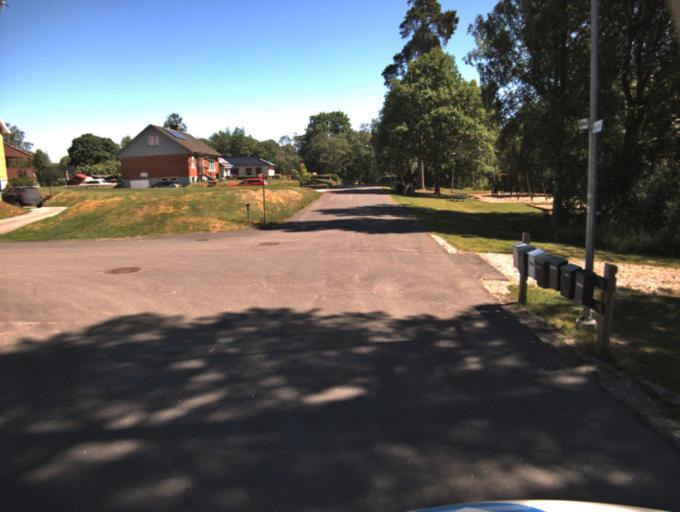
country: SE
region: Vaestra Goetaland
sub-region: Ulricehamns Kommun
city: Ulricehamn
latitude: 57.6652
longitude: 13.4244
